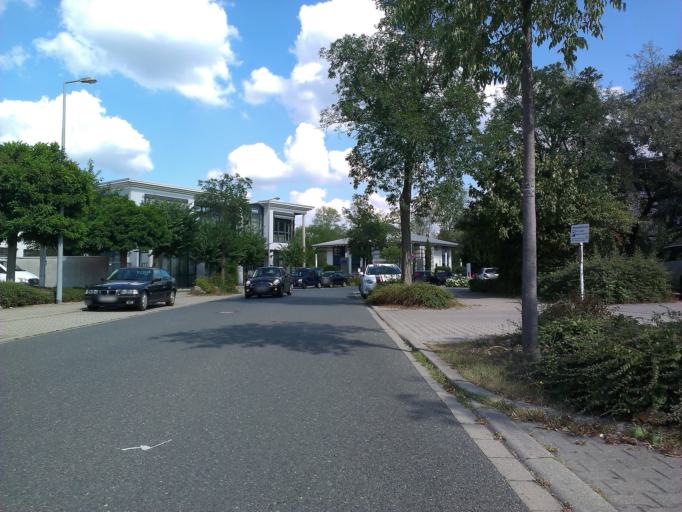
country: DE
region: Baden-Wuerttemberg
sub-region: Karlsruhe Region
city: Mannheim
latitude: 49.5354
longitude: 8.4789
